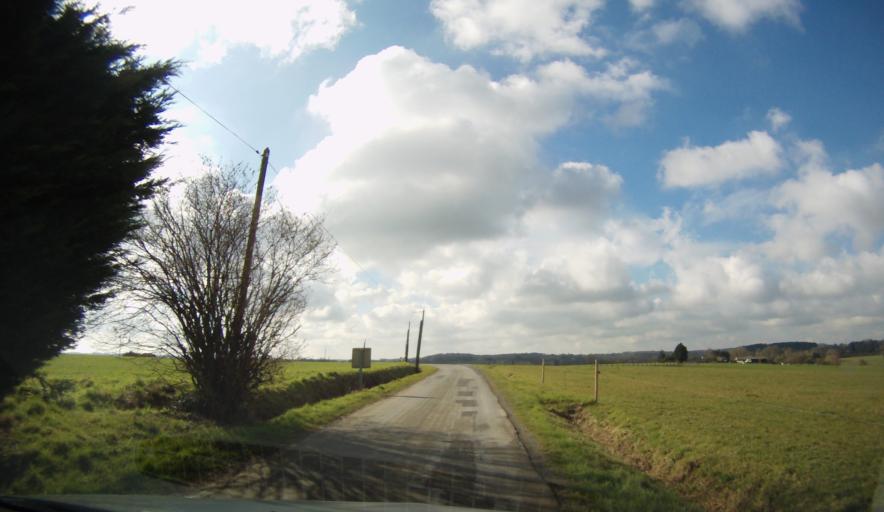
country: FR
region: Brittany
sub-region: Departement d'Ille-et-Vilaine
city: Chanteloup
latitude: 47.9601
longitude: -1.5997
